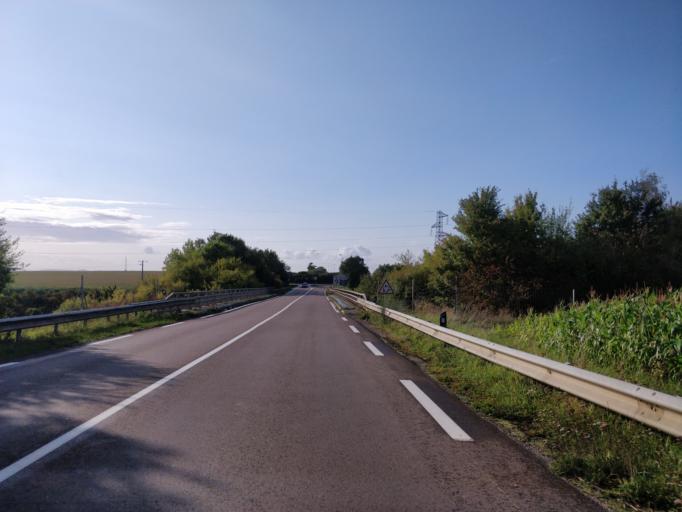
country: FR
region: Champagne-Ardenne
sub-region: Departement de l'Aube
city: Saint-Parres-aux-Tertres
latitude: 48.2861
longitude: 4.1656
